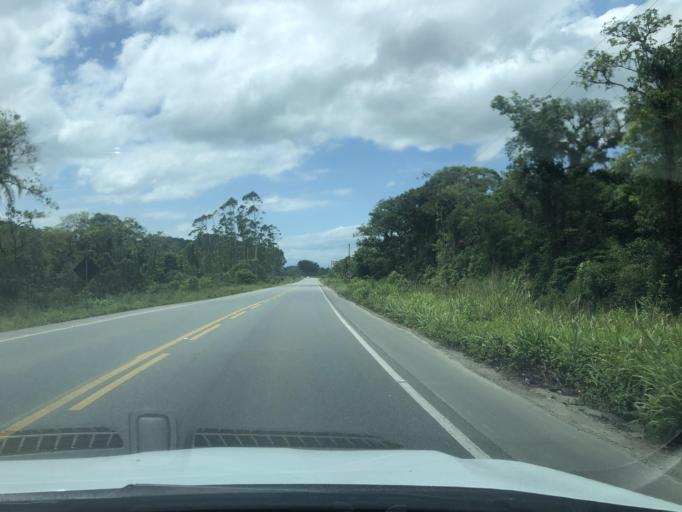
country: BR
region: Santa Catarina
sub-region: Joinville
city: Joinville
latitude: -26.3966
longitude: -48.7639
